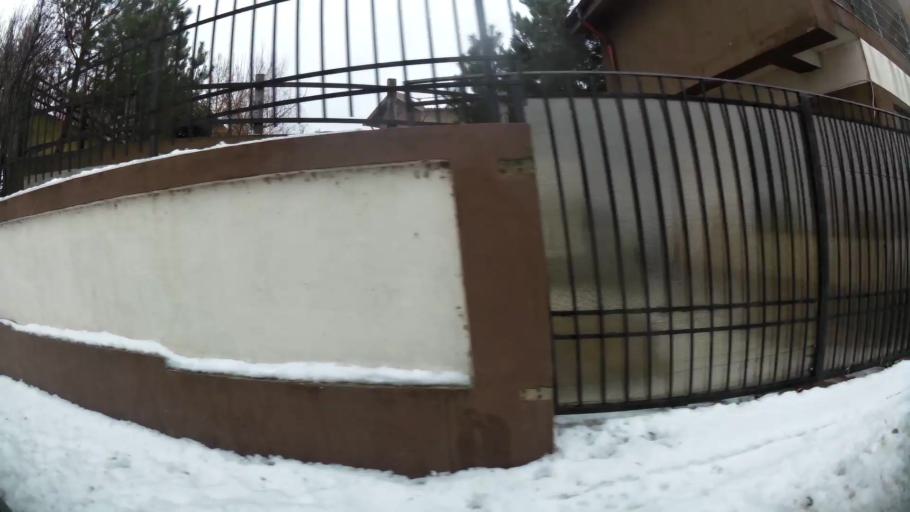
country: RO
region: Ilfov
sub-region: Comuna Chiajna
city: Rosu
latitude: 44.4496
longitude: 26.0147
